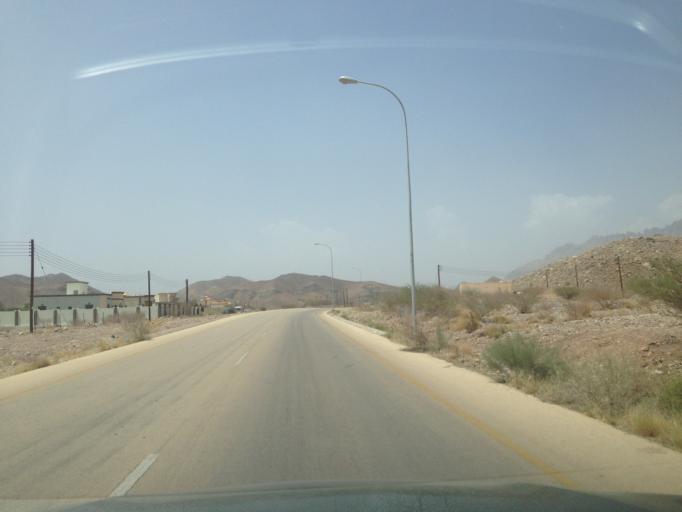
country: OM
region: Az Zahirah
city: `Ibri
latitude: 23.1773
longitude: 56.9189
